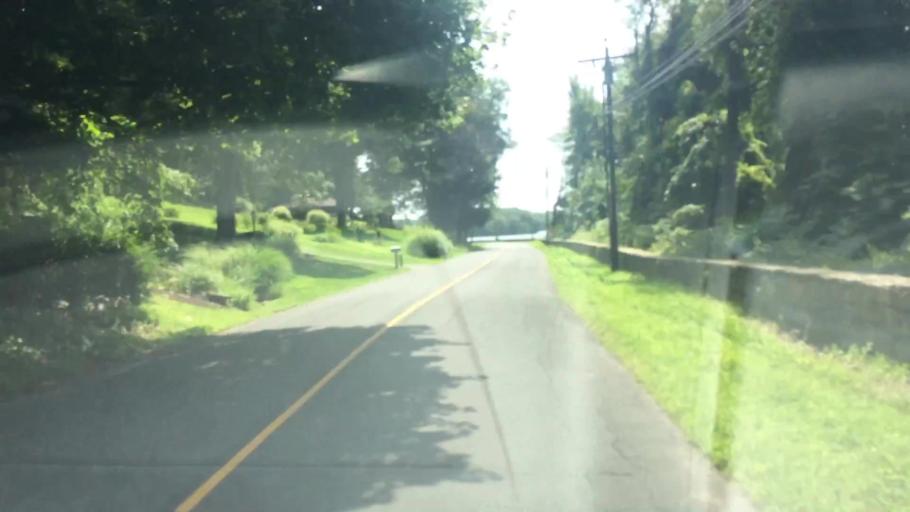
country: US
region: Connecticut
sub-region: Fairfield County
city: Danbury
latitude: 41.4127
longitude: -73.5089
